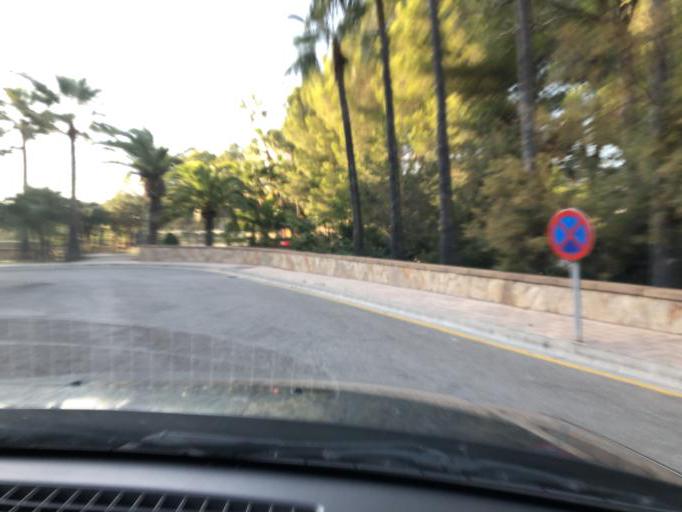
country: ES
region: Balearic Islands
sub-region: Illes Balears
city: Santa Ponsa
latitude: 39.5353
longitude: 2.4608
